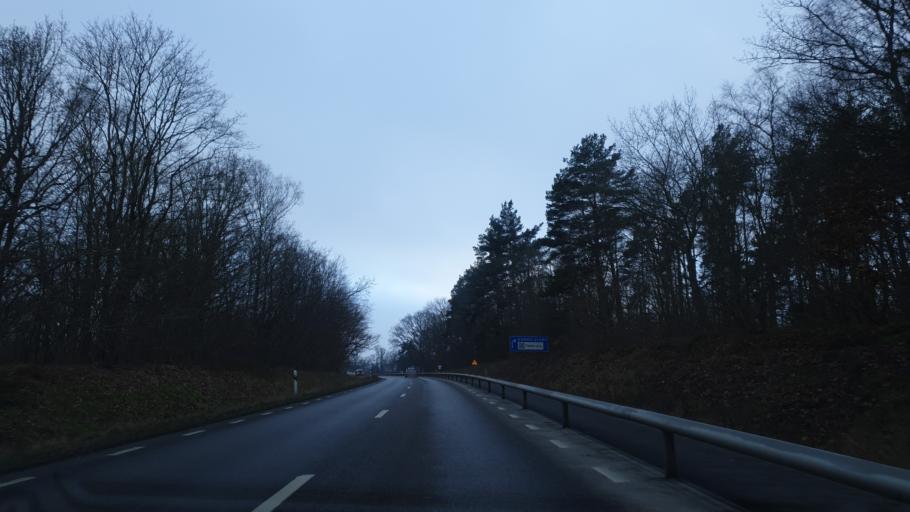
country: SE
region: Blekinge
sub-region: Solvesborgs Kommun
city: Soelvesborg
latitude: 56.0930
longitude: 14.6545
